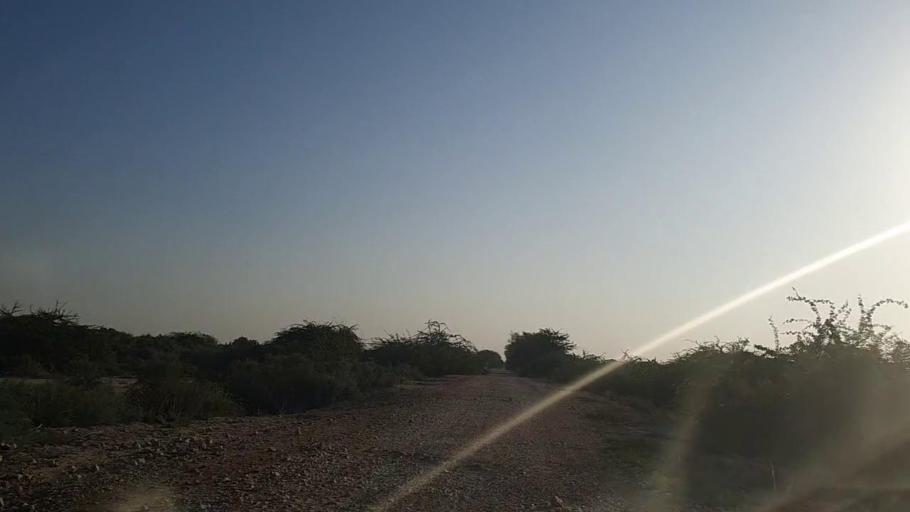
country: PK
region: Sindh
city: Jati
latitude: 24.4286
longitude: 68.1898
